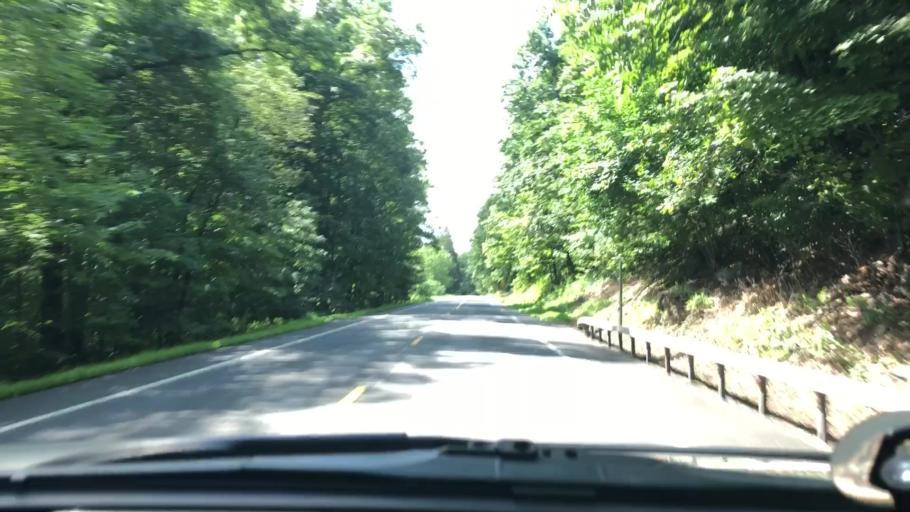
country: US
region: New York
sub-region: Greene County
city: Palenville
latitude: 42.2019
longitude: -73.9849
